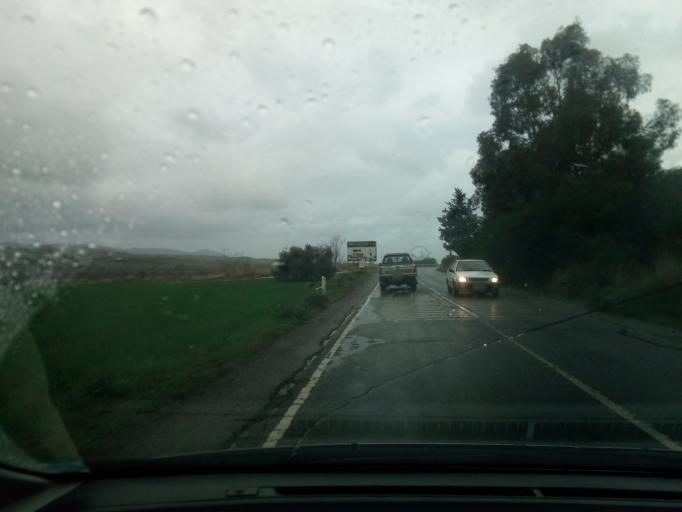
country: CY
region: Pafos
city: Polis
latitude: 35.0080
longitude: 32.4380
